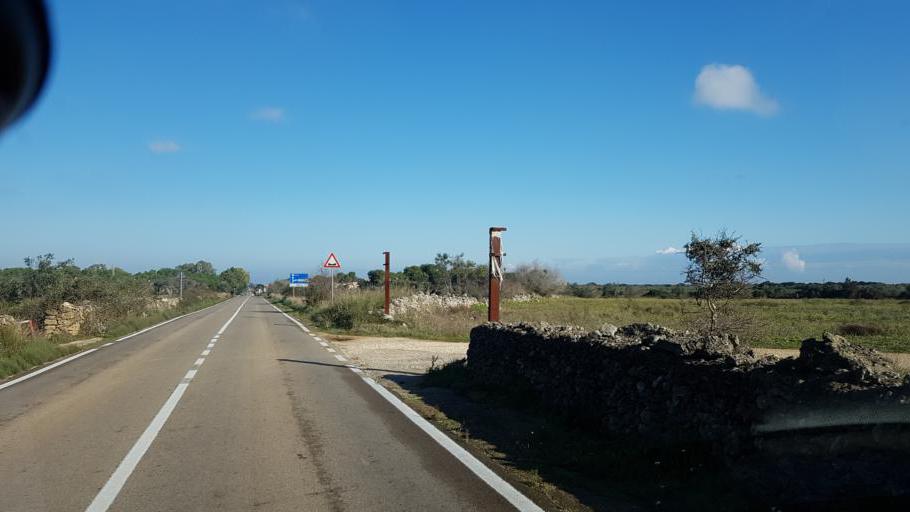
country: IT
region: Apulia
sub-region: Provincia di Lecce
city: Trepuzzi
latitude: 40.4546
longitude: 18.1125
